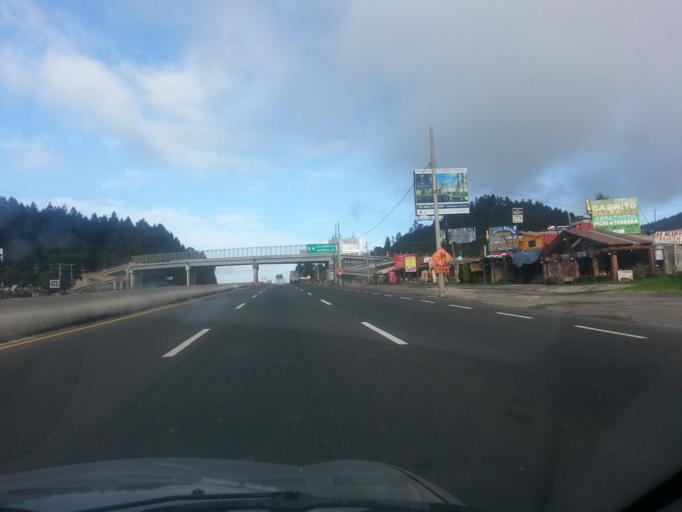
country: MX
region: Morelos
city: San Jeronimo Acazulco
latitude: 19.2995
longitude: -99.3900
